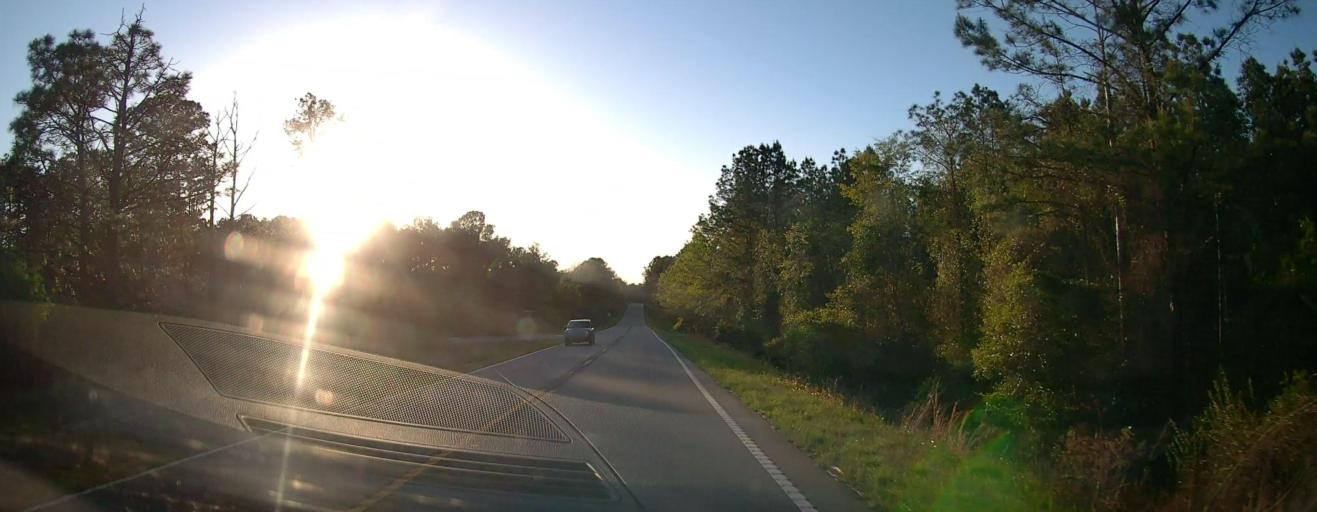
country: US
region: Georgia
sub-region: Talbot County
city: Talbotton
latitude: 32.5406
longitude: -84.5228
